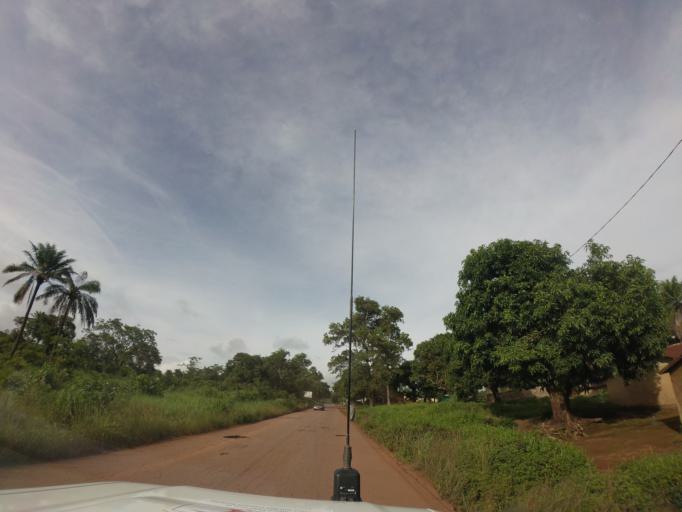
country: GN
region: Kindia
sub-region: Kindia
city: Kindia
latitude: 9.8588
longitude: -13.0823
